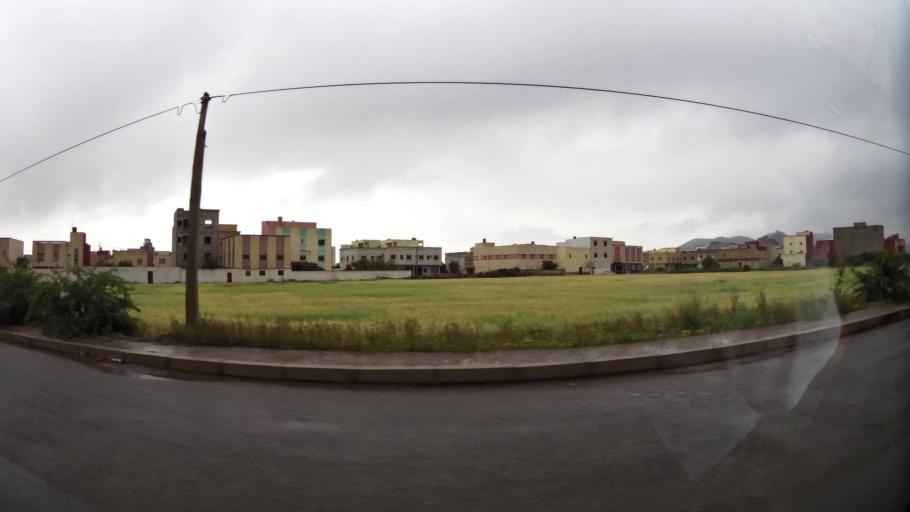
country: MA
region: Oriental
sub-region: Nador
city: Nador
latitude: 35.1559
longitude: -2.9737
